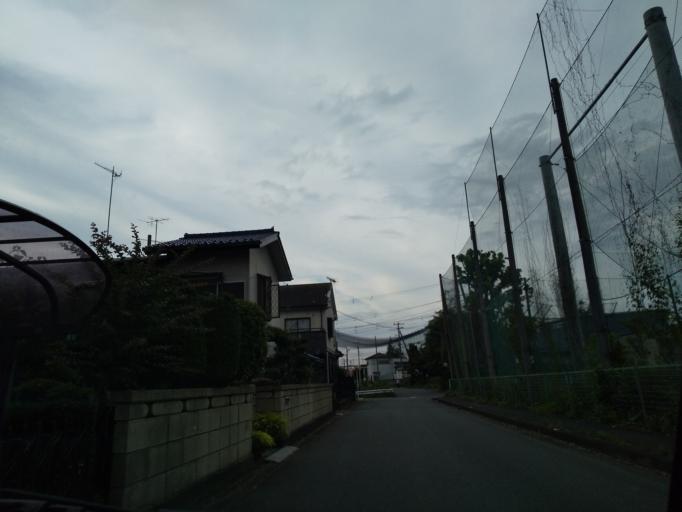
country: JP
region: Kanagawa
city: Atsugi
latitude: 35.4702
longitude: 139.3617
